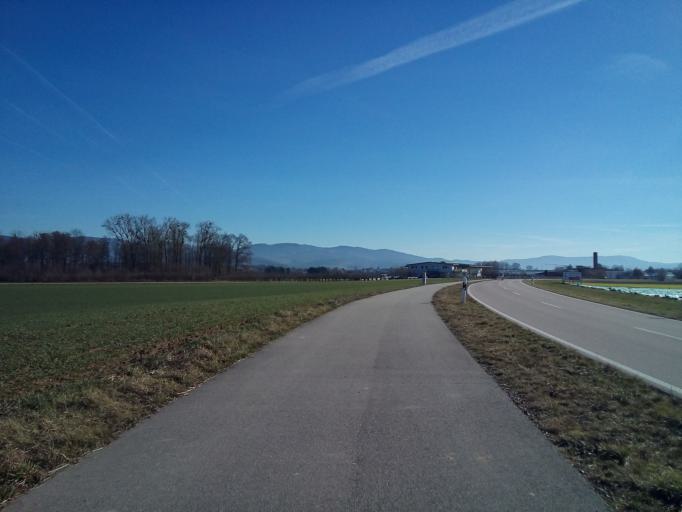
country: DE
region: Baden-Wuerttemberg
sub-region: Freiburg Region
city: Renchen
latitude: 48.6192
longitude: 8.0176
